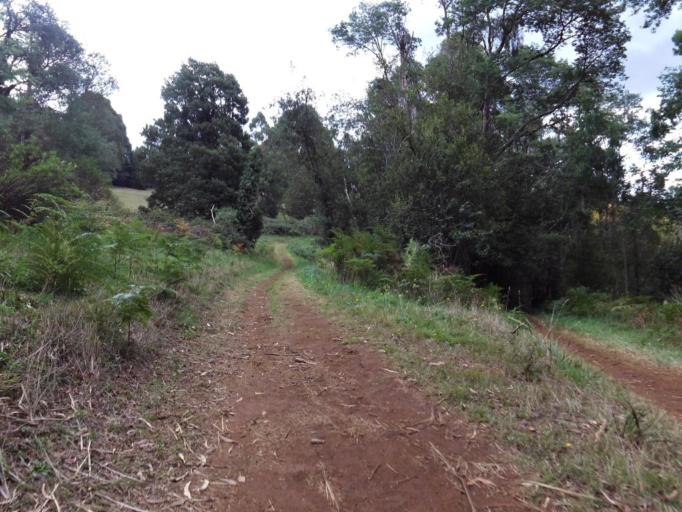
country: AU
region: Victoria
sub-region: Yarra Ranges
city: Olinda
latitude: -37.8521
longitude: 145.3786
